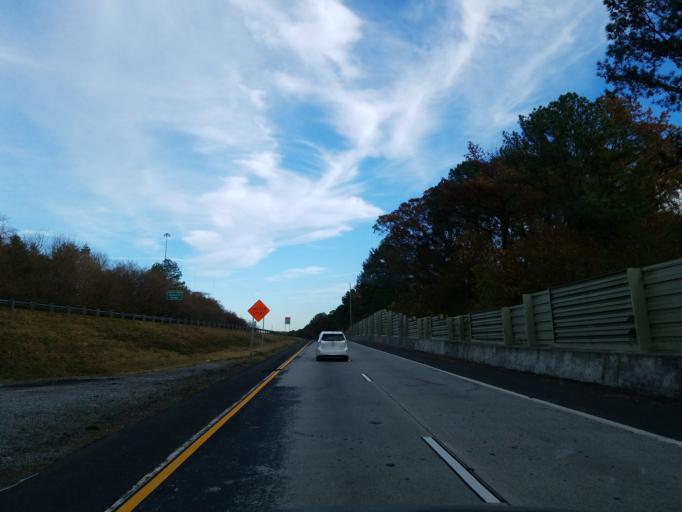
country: US
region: Georgia
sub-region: Fulton County
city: East Point
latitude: 33.7607
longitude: -84.4872
